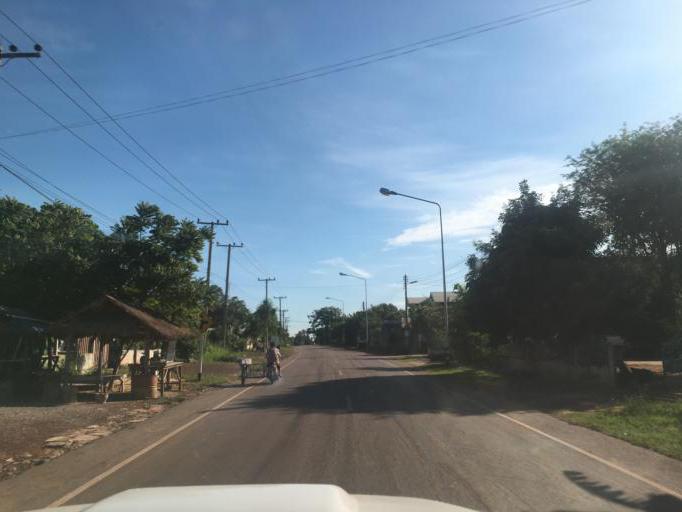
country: TH
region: Changwat Udon Thani
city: Kut Chap
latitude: 17.4709
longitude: 102.5896
